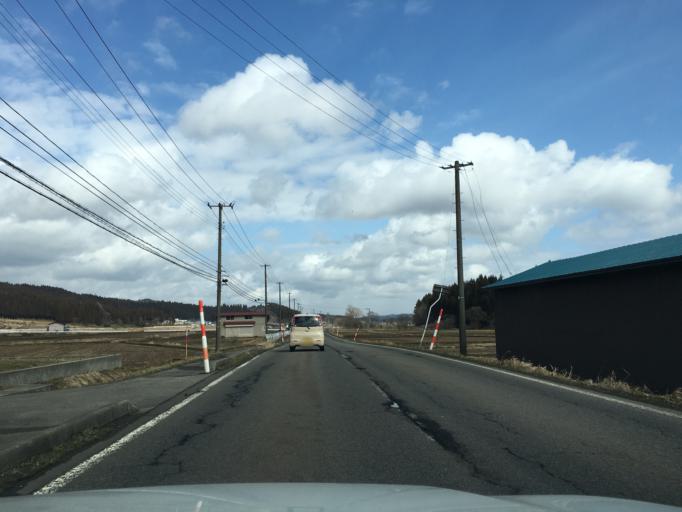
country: JP
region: Akita
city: Takanosu
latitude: 40.0355
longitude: 140.2762
